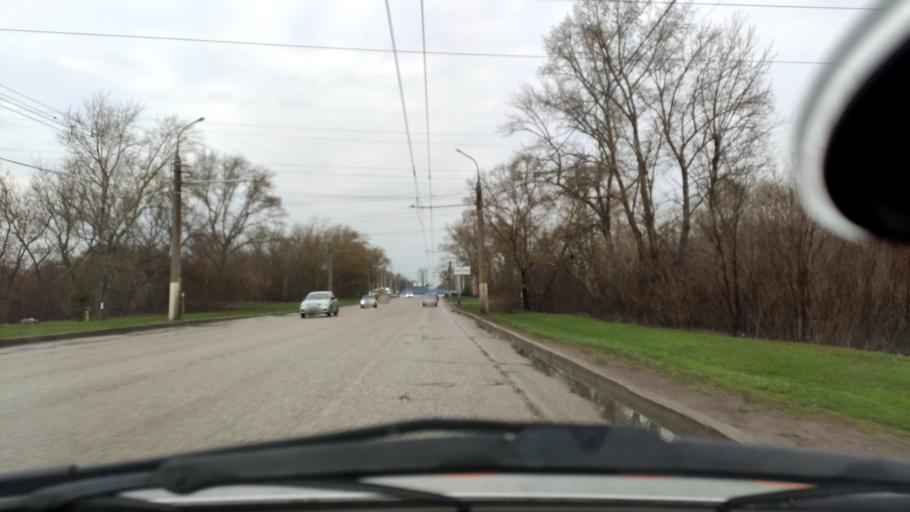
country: RU
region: Bashkortostan
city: Sterlitamak
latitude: 53.6603
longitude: 55.9489
